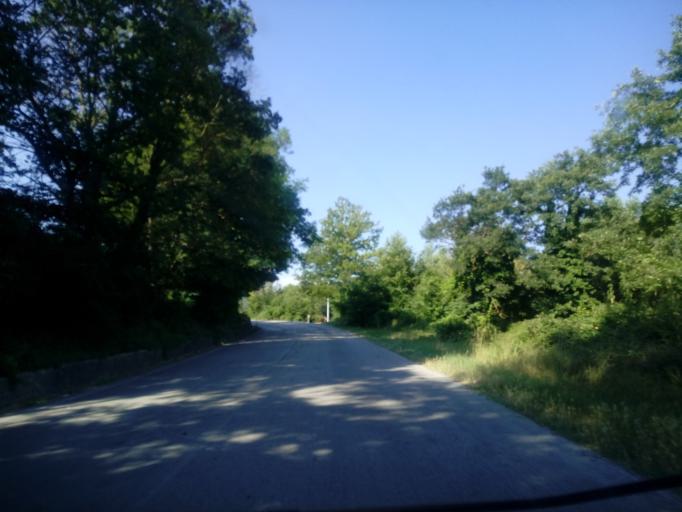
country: IT
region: Molise
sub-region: Provincia di Campobasso
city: Jelsi
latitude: 41.5130
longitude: 14.7898
